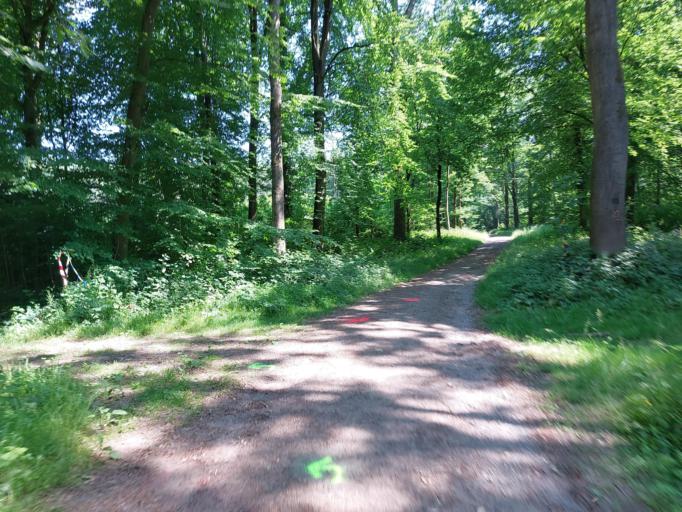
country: BE
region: Wallonia
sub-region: Province du Hainaut
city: Roeulx
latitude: 50.4614
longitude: 4.0620
